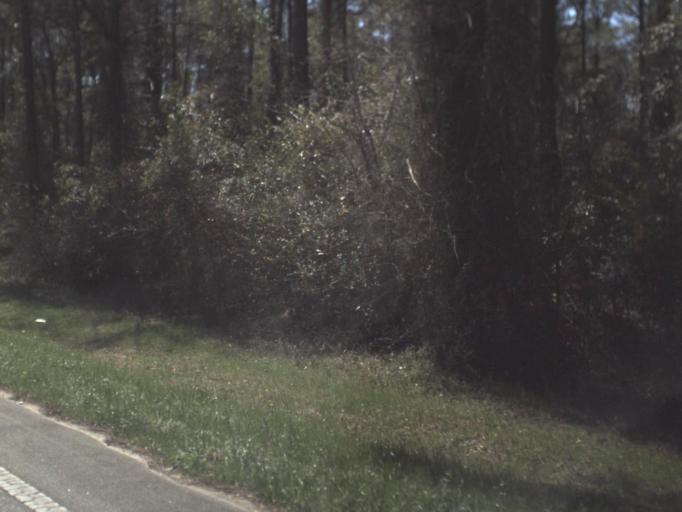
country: US
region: Florida
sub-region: Gadsden County
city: Quincy
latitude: 30.6413
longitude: -84.6000
